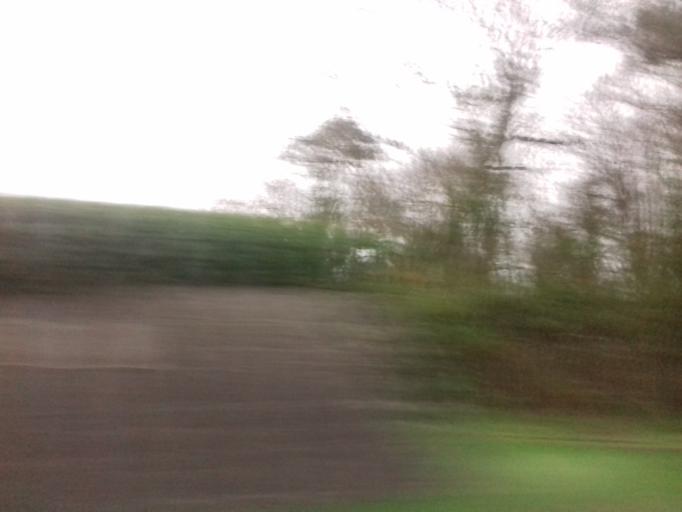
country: IE
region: Munster
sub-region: County Limerick
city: Adare
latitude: 52.5517
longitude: -8.8117
